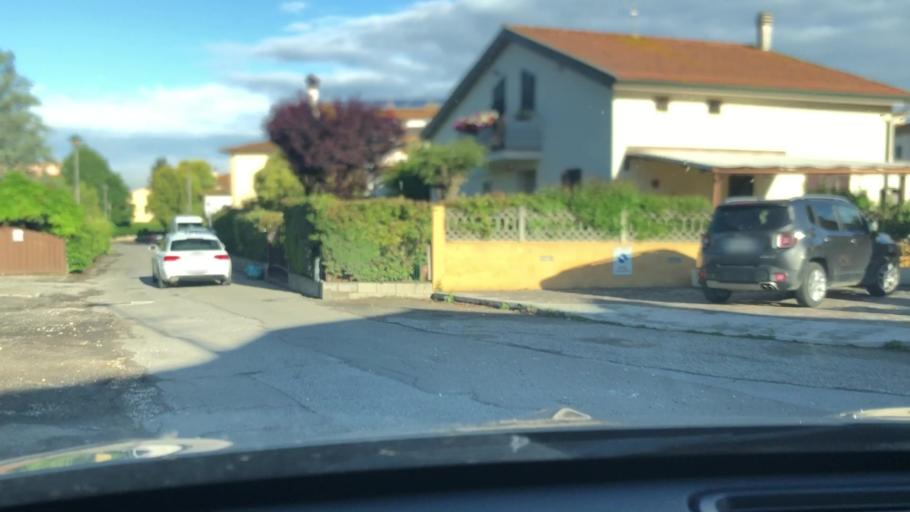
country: IT
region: Tuscany
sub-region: Province of Pisa
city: Forcoli
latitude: 43.6032
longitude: 10.7016
